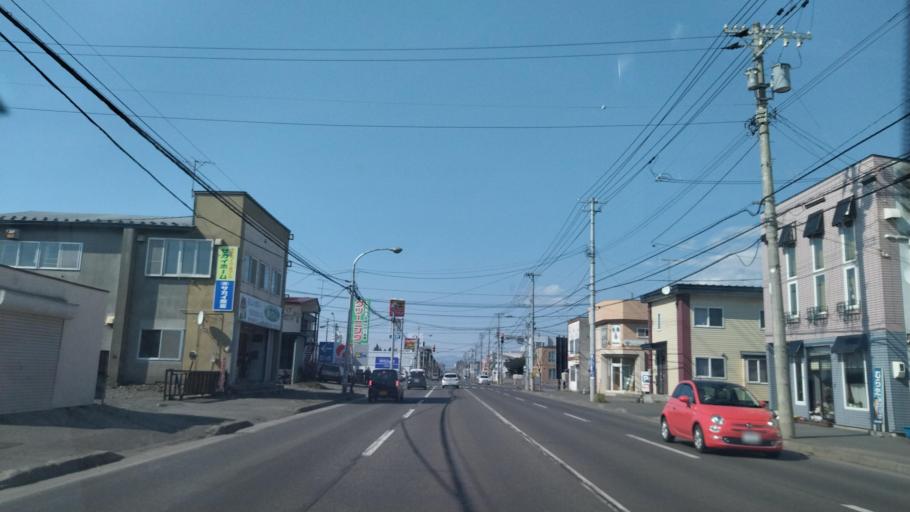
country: JP
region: Hokkaido
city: Obihiro
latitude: 42.8980
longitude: 143.2006
